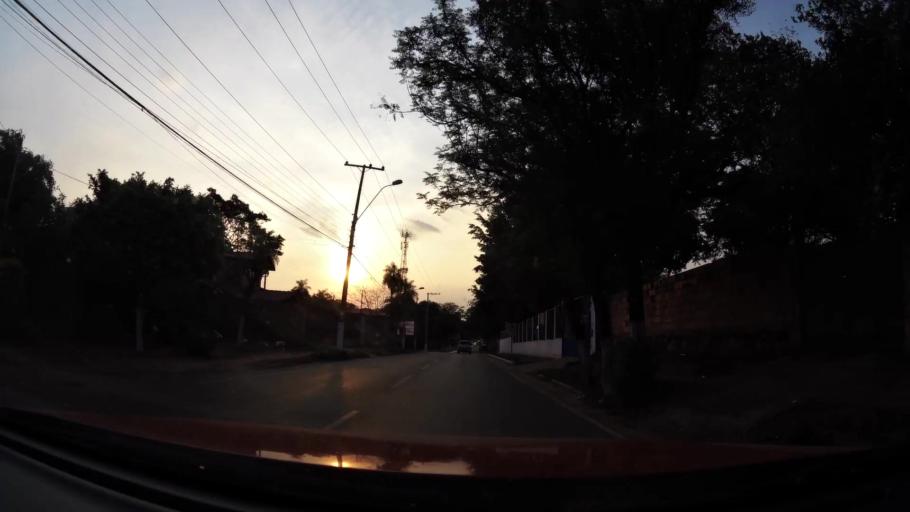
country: PY
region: Central
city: Lambare
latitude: -25.3565
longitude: -57.6007
